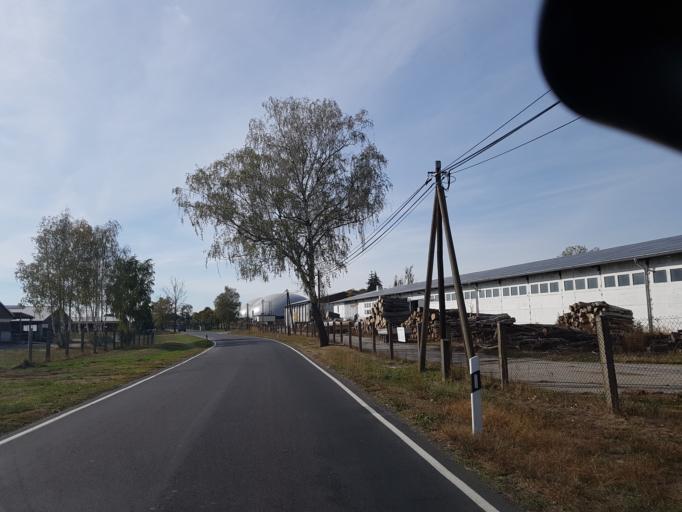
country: DE
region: Brandenburg
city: Schlieben
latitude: 51.7166
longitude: 13.4130
